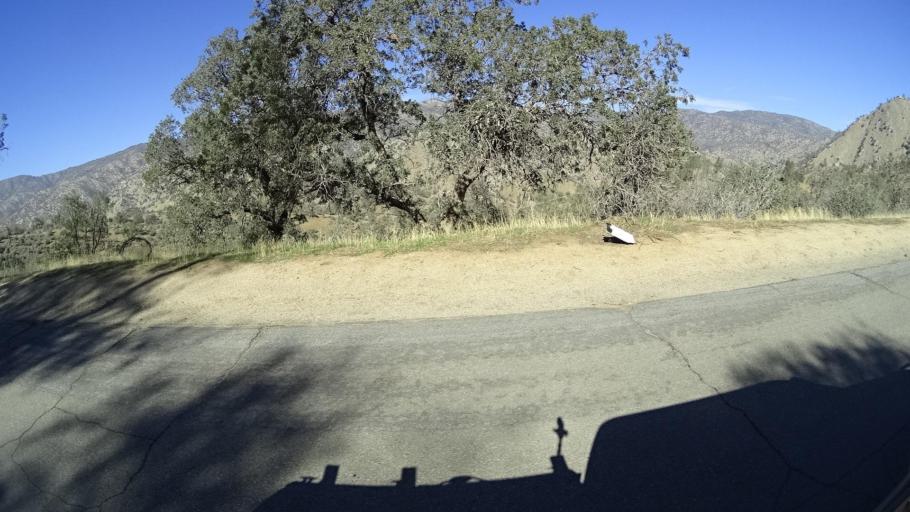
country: US
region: California
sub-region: Kern County
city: Bodfish
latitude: 35.5299
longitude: -118.6242
